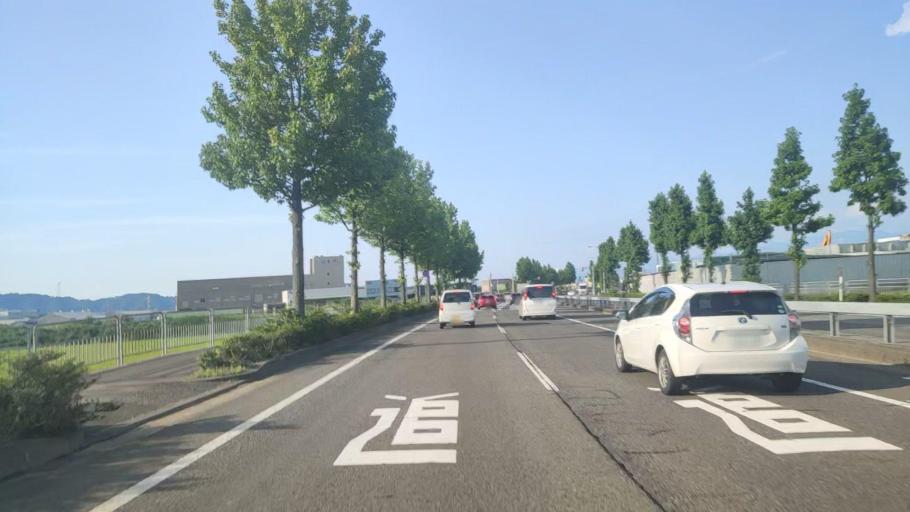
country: JP
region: Fukui
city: Fukui-shi
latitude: 36.0170
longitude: 136.2107
